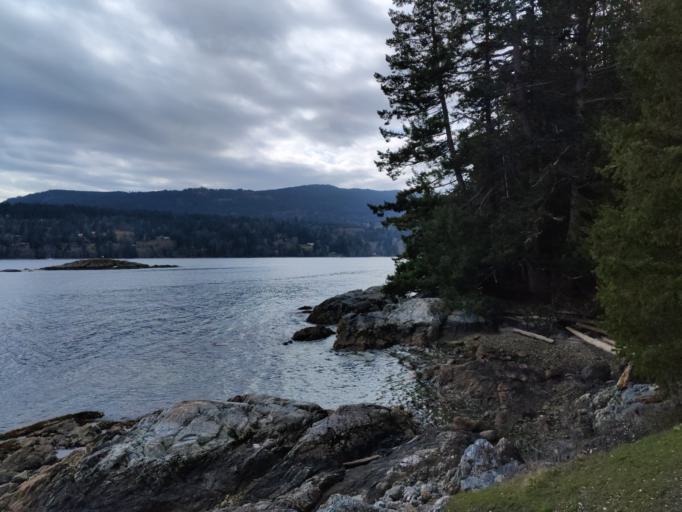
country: CA
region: British Columbia
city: North Saanich
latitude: 48.7551
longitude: -123.4260
